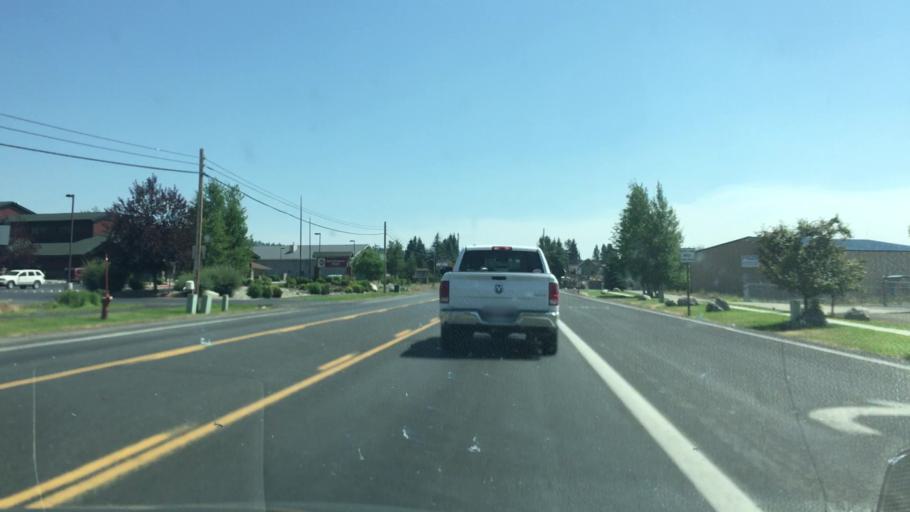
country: US
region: Idaho
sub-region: Valley County
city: McCall
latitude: 44.8967
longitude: -116.0961
